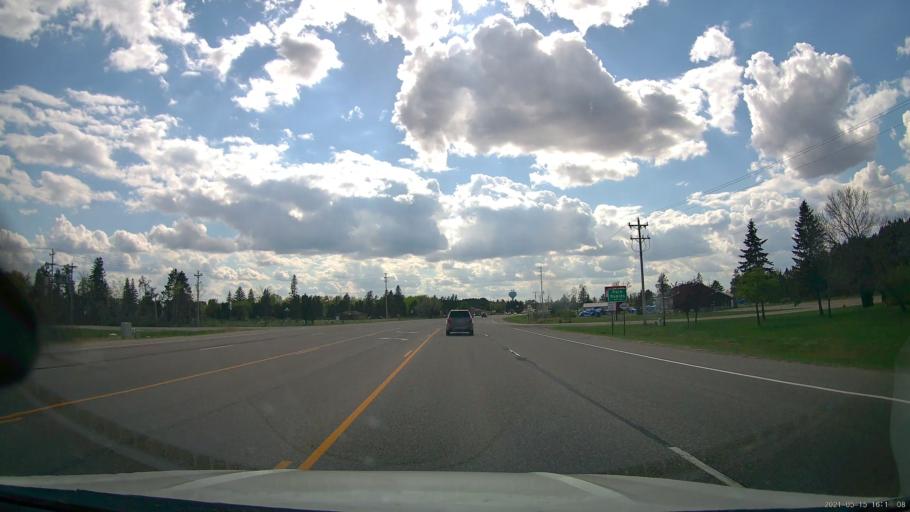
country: US
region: Minnesota
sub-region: Hubbard County
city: Park Rapids
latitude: 46.9225
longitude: -95.0270
